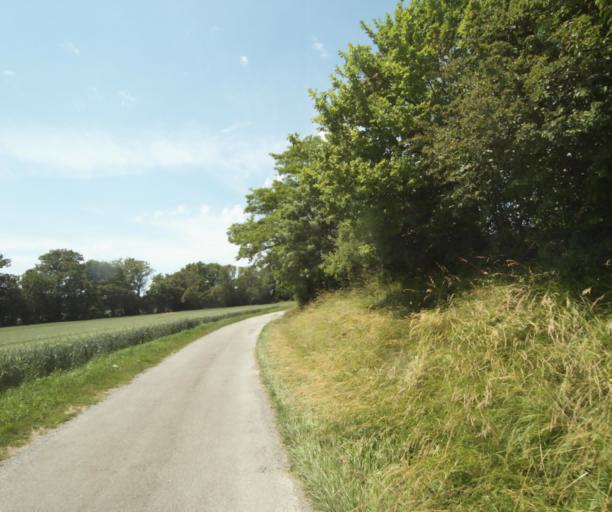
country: FR
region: Rhone-Alpes
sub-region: Departement de la Haute-Savoie
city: Messery
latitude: 46.3647
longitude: 6.3297
